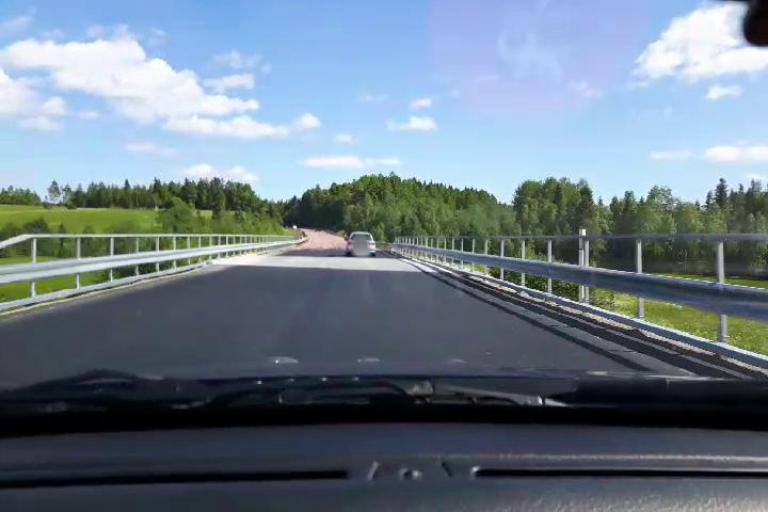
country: SE
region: Gaevleborg
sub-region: Hudiksvalls Kommun
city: Sorforsa
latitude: 61.7424
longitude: 16.8577
